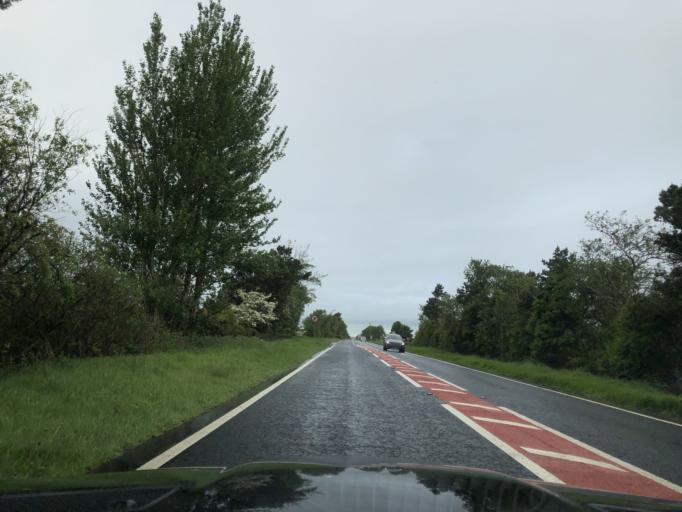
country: GB
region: Northern Ireland
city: Dunloy
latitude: 55.0357
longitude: -6.4083
